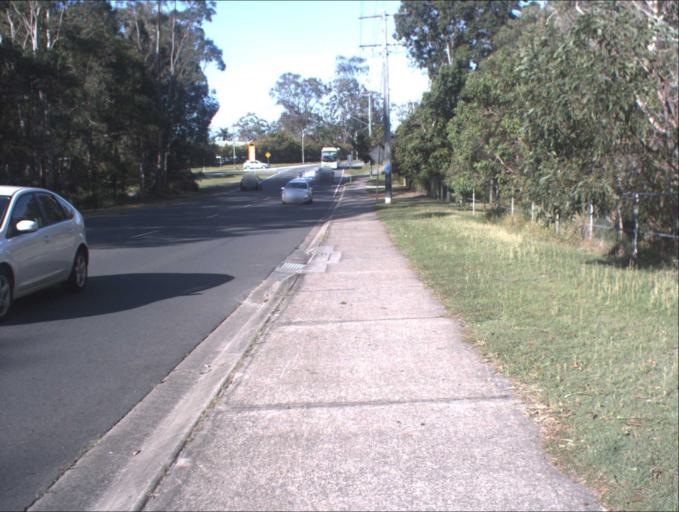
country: AU
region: Queensland
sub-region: Logan
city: Park Ridge South
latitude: -27.6992
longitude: 153.0312
